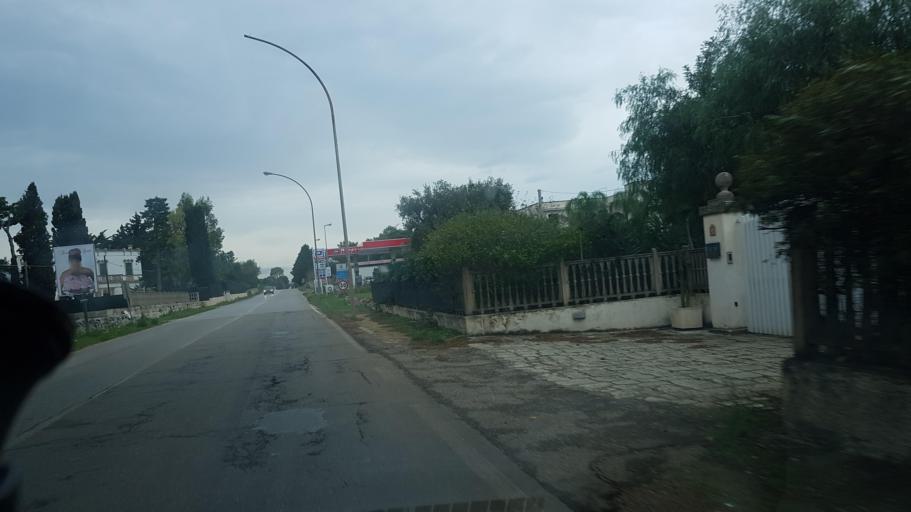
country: IT
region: Apulia
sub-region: Provincia di Brindisi
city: Carovigno
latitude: 40.7075
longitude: 17.6459
